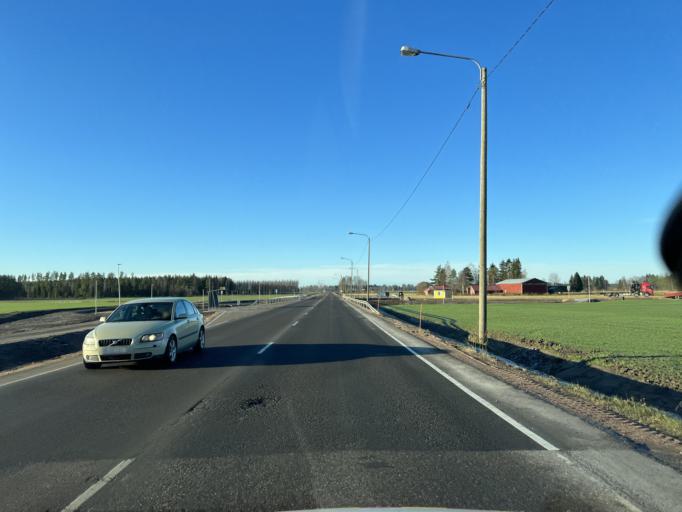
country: FI
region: Northern Ostrobothnia
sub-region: Nivala-Haapajaervi
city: Nivala
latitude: 63.9512
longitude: 24.9017
